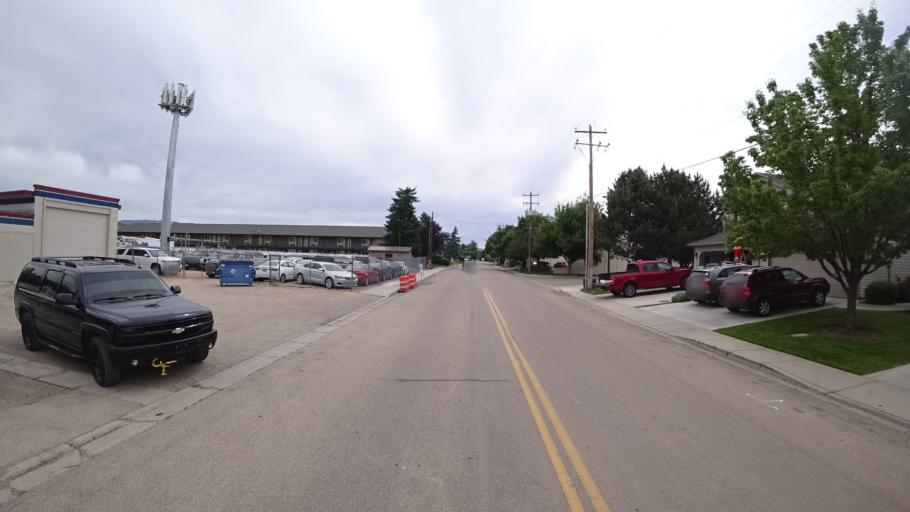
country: US
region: Idaho
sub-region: Ada County
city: Boise
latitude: 43.5772
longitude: -116.2158
